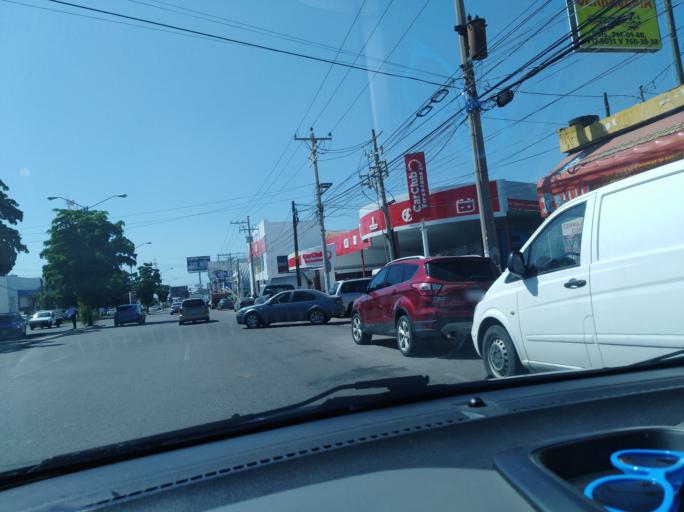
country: MX
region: Sinaloa
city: Culiacan
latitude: 24.7931
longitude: -107.4151
